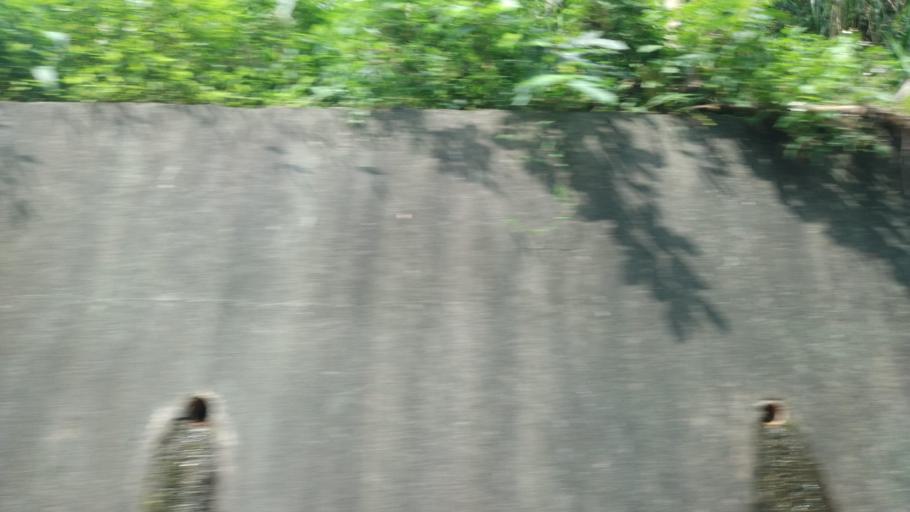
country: TW
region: Taiwan
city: Daxi
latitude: 24.9092
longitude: 121.4033
